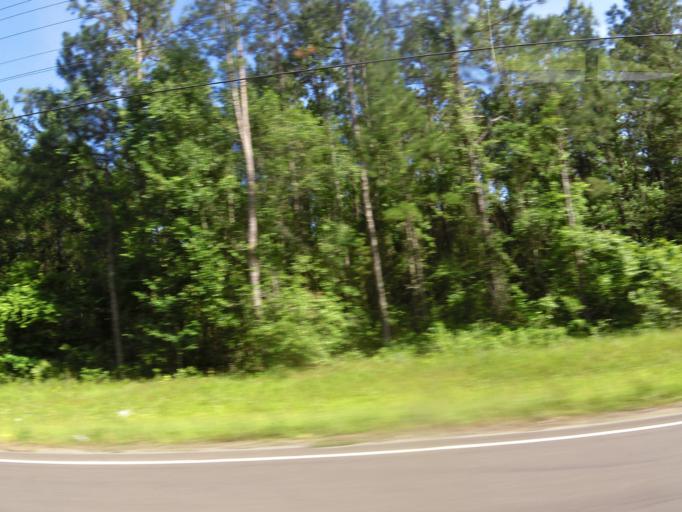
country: US
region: Florida
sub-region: Nassau County
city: Callahan
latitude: 30.5605
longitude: -81.8534
